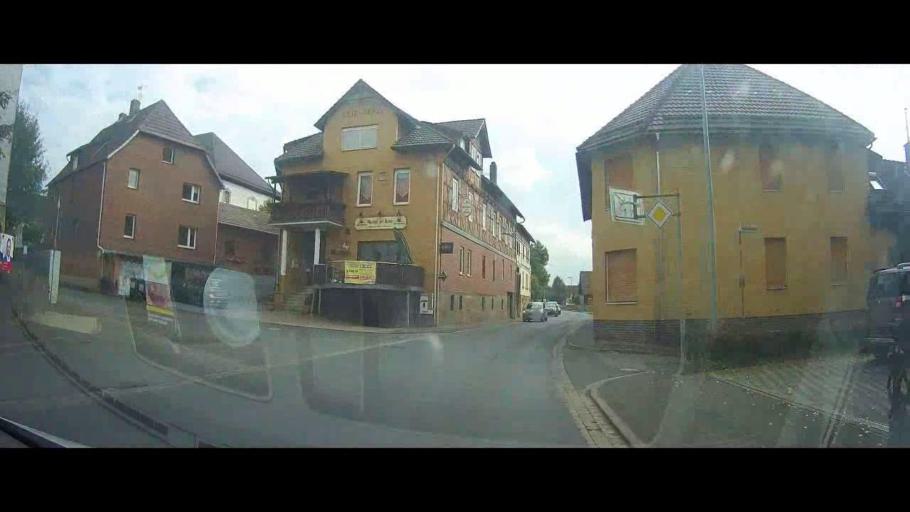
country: DE
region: Lower Saxony
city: Uslar
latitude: 51.6304
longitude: 9.6593
